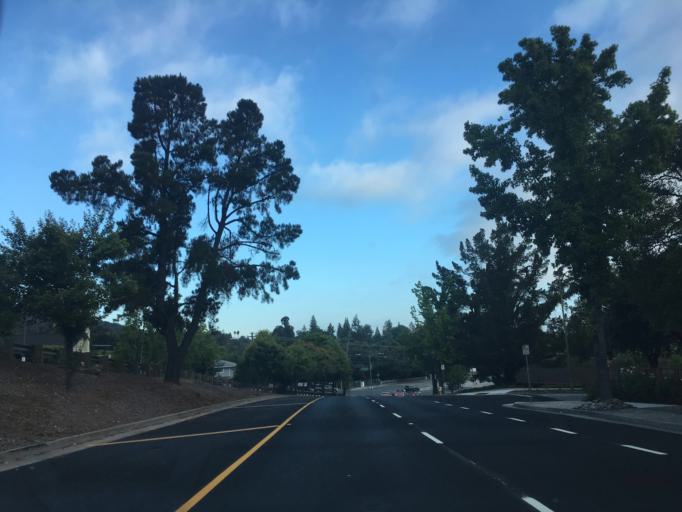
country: US
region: California
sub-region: Santa Clara County
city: Cambrian Park
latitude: 37.2249
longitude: -121.9021
